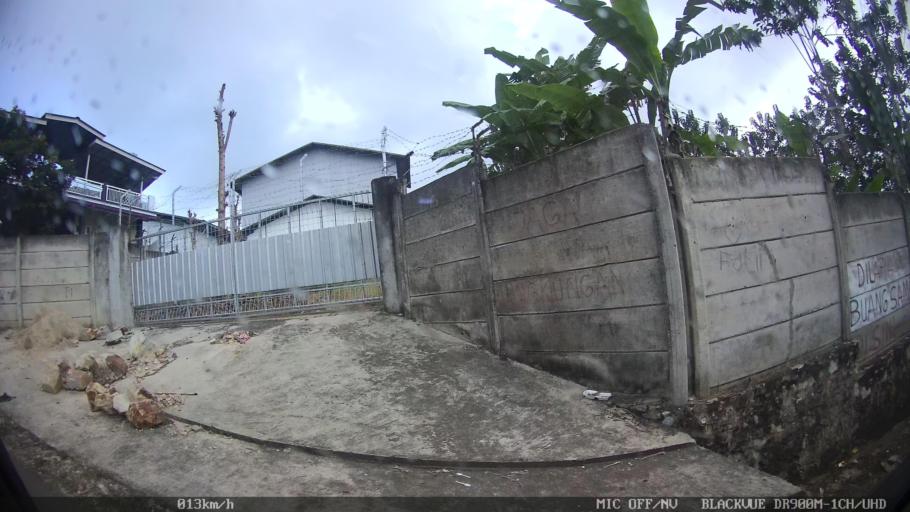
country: ID
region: Lampung
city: Bandarlampung
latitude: -5.4194
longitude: 105.2925
